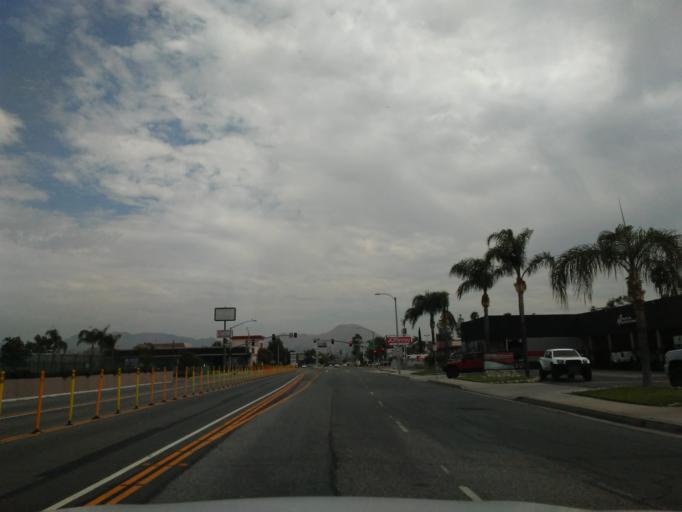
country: US
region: California
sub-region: San Bernardino County
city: San Bernardino
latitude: 34.0867
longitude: -117.2939
